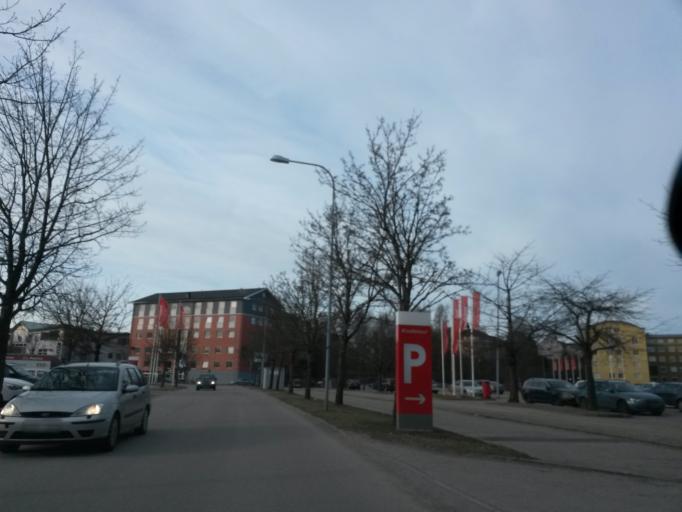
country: SE
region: Vaestra Goetaland
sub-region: Boras Kommun
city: Boras
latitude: 57.7333
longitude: 12.9417
